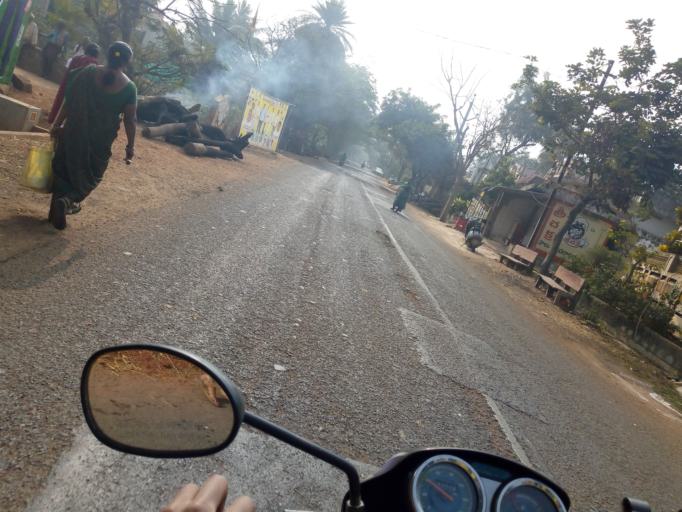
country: IN
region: Andhra Pradesh
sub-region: West Godavari
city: Tadepallegudem
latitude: 16.7800
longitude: 81.4207
